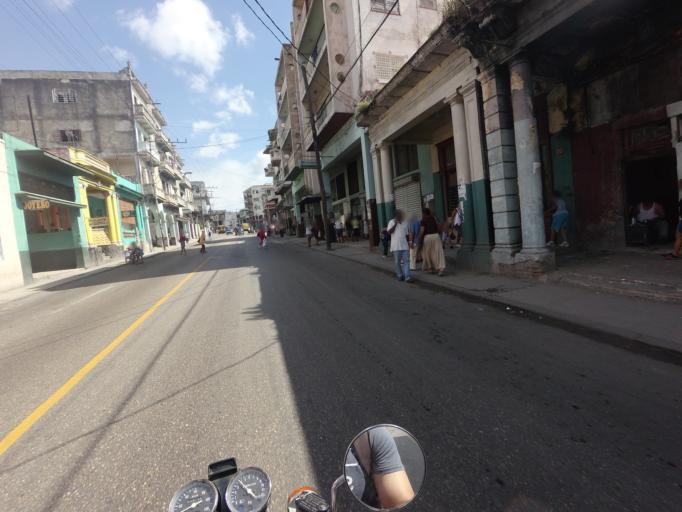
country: TM
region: Balkan
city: Gumdag
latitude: 38.8438
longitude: 54.1729
